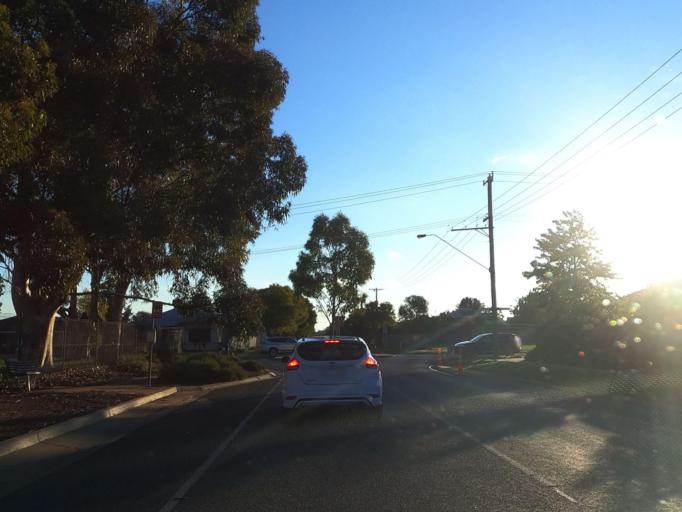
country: AU
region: Victoria
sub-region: Swan Hill
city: Swan Hill
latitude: -35.3477
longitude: 143.5559
